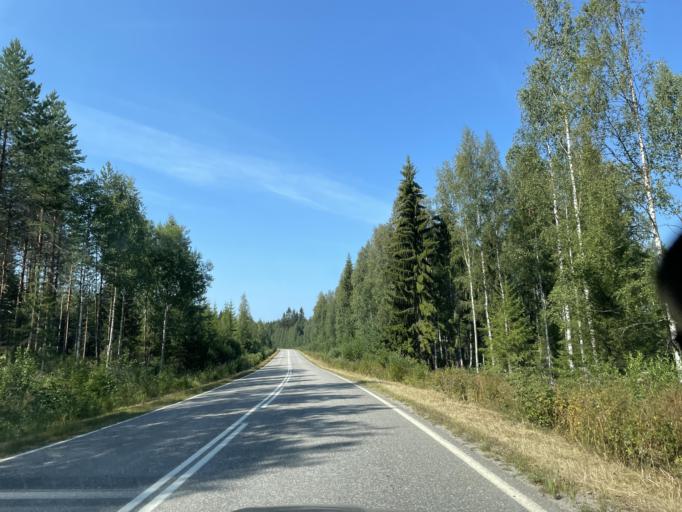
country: FI
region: Central Finland
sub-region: Saarijaervi-Viitasaari
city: Pihtipudas
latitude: 63.3675
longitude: 25.6886
